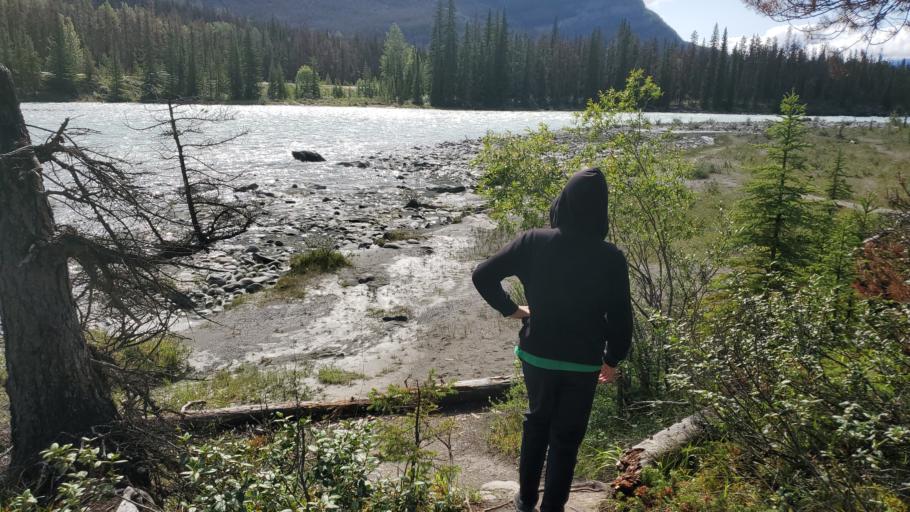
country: CA
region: Alberta
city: Jasper Park Lodge
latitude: 52.6630
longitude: -117.8811
